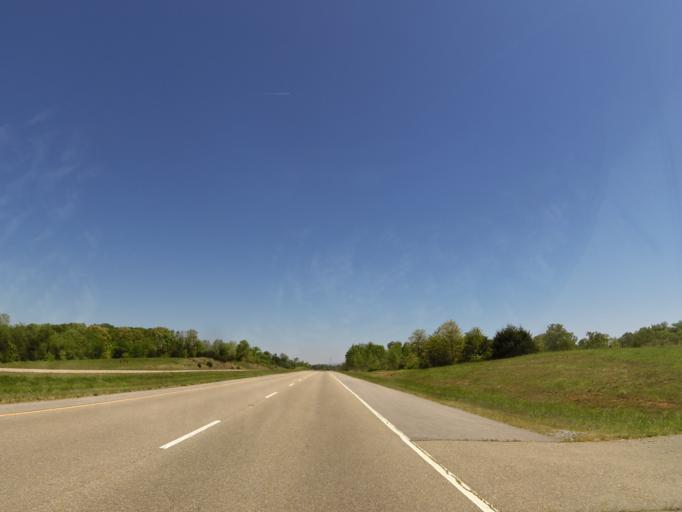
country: US
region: Tennessee
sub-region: Greene County
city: Mosheim
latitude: 36.0347
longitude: -83.0213
